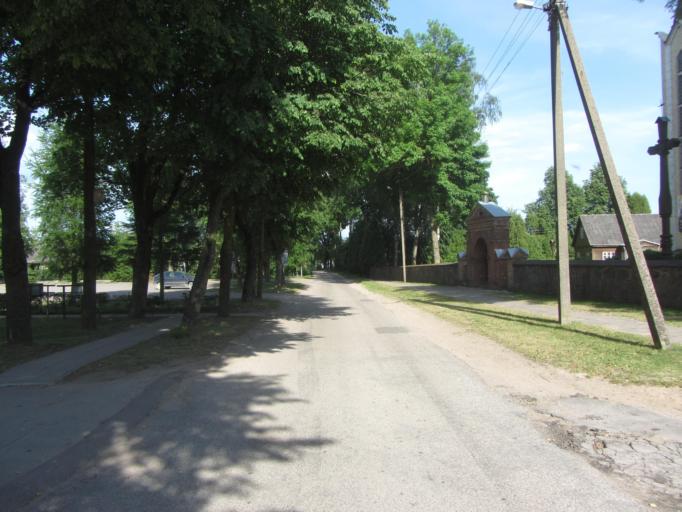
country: LT
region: Kauno apskritis
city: Jonava
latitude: 55.1967
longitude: 24.4343
